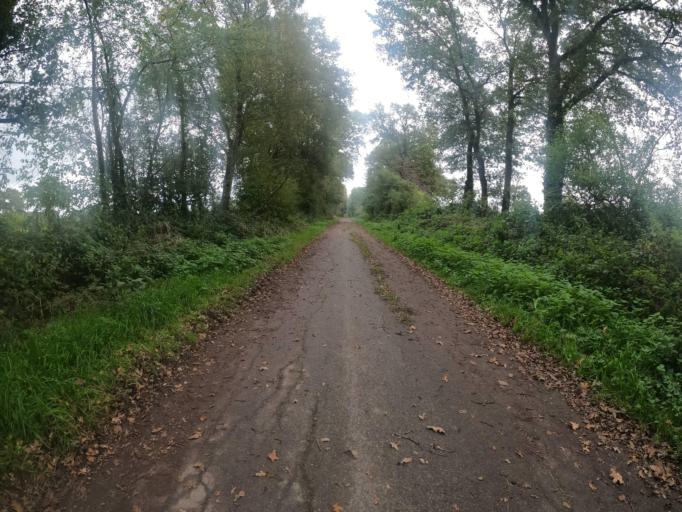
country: DE
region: North Rhine-Westphalia
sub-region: Regierungsbezirk Munster
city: Raesfeld
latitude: 51.7232
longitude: 6.8454
